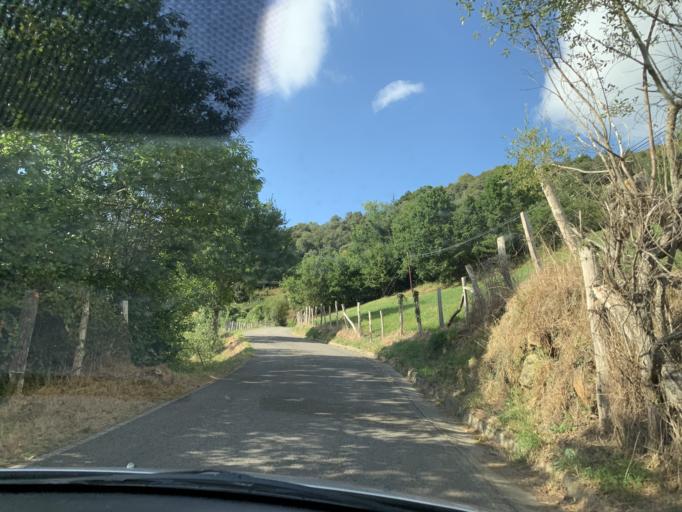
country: ES
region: Asturias
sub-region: Province of Asturias
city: Carrena
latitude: 43.3207
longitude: -4.8545
